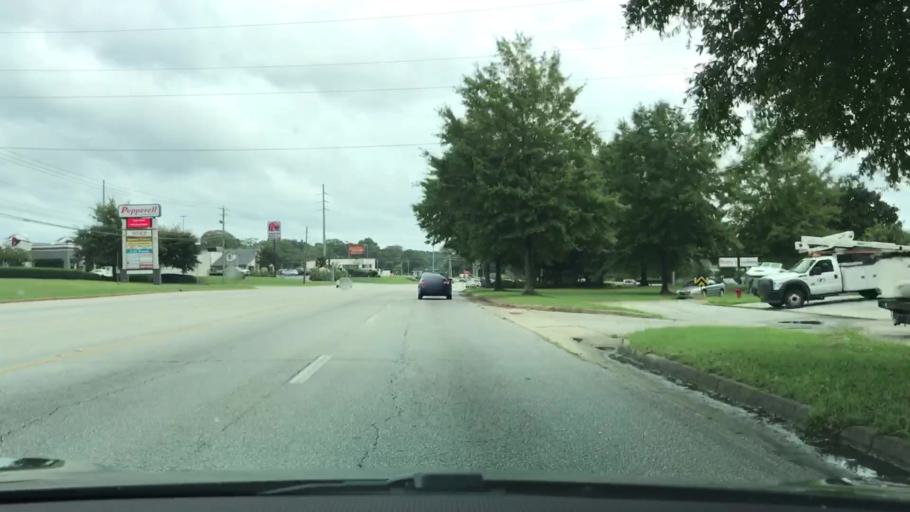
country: US
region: Alabama
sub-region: Lee County
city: Opelika
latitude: 32.6377
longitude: -85.4128
